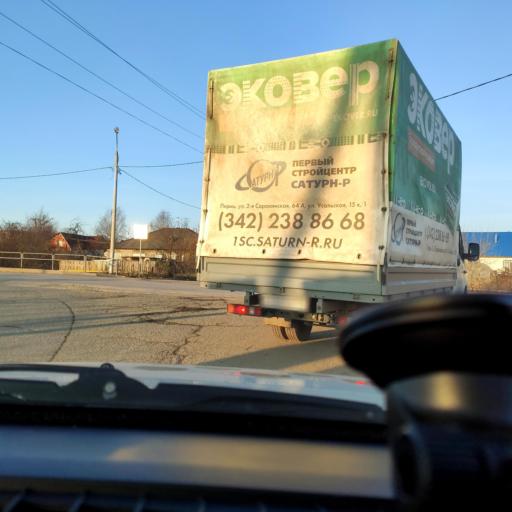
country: RU
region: Perm
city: Ferma
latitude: 57.9563
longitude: 56.3712
